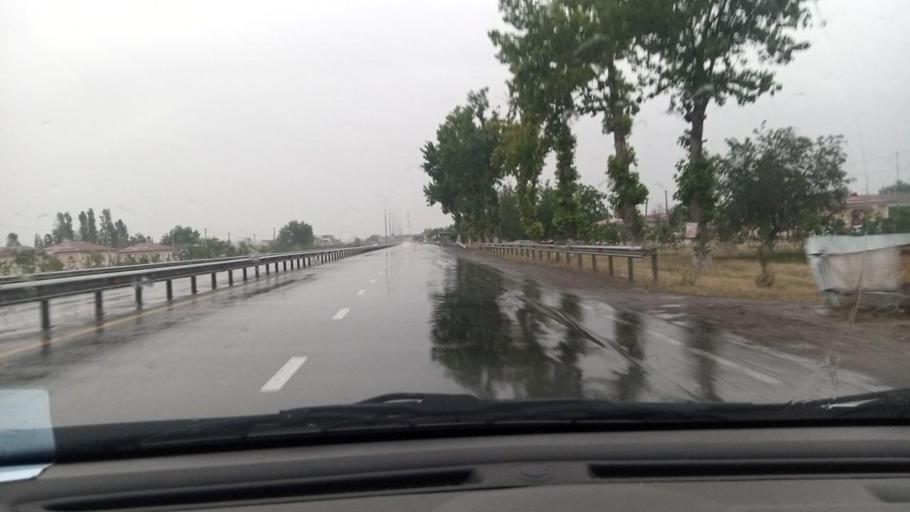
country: UZ
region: Toshkent Shahri
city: Bektemir
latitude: 41.1352
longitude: 69.4348
